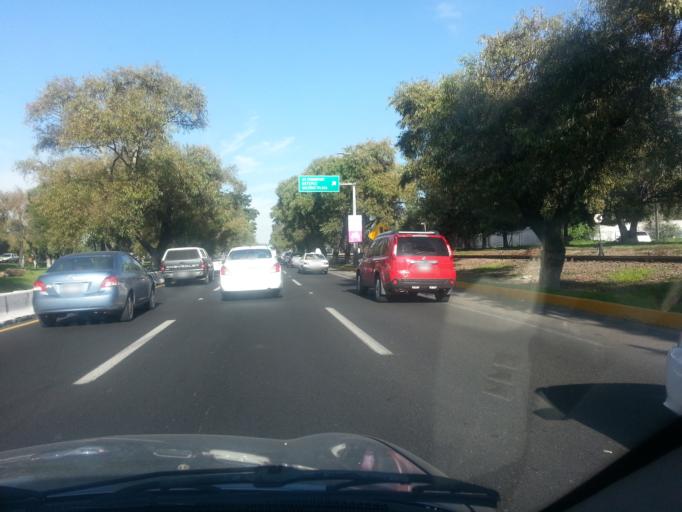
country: MX
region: Mexico
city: Santa Maria Totoltepec
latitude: 19.2876
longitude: -99.6015
